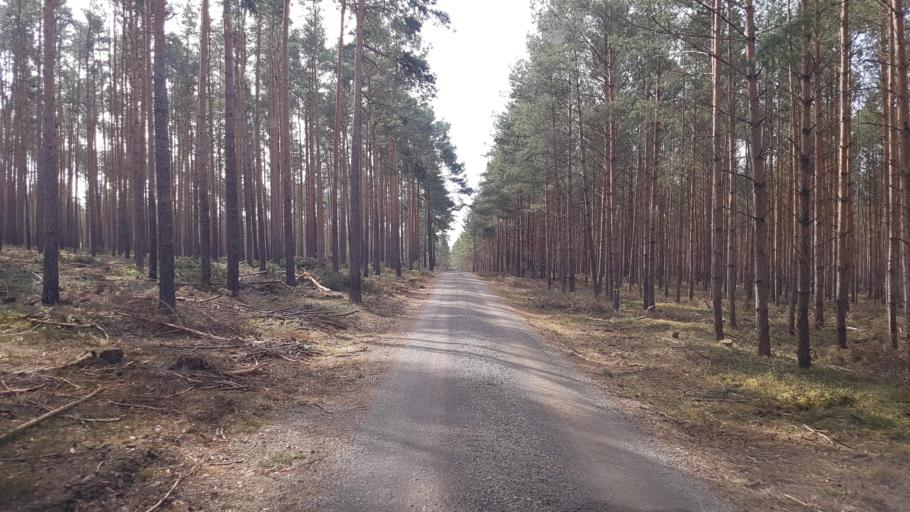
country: DE
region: Brandenburg
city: Elsterwerda
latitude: 51.4931
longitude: 13.4600
